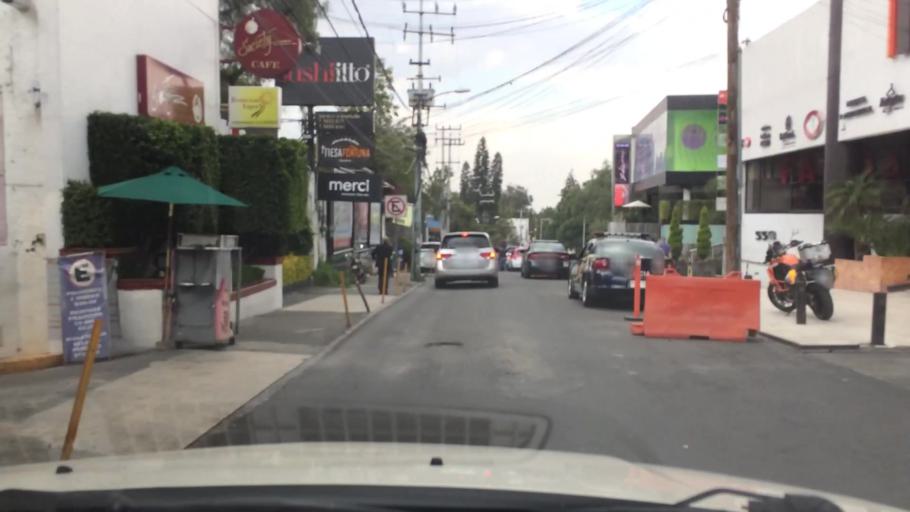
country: MX
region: Mexico City
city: Magdalena Contreras
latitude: 19.3162
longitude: -99.2124
